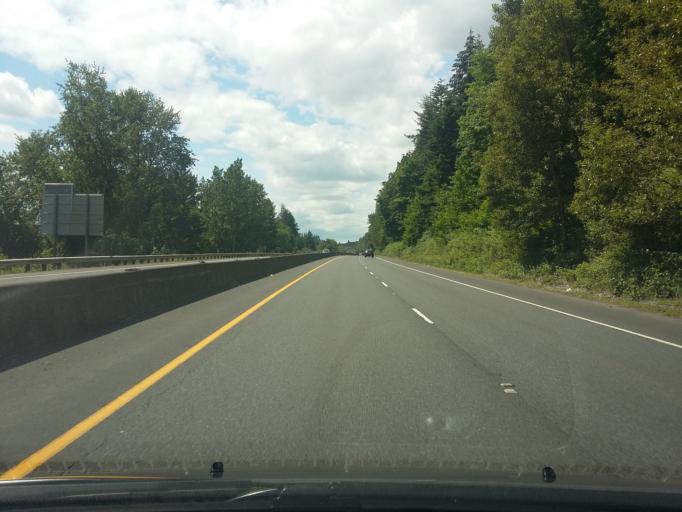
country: US
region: Oregon
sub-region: Multnomah County
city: Fairview
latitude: 45.5805
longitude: -122.4544
